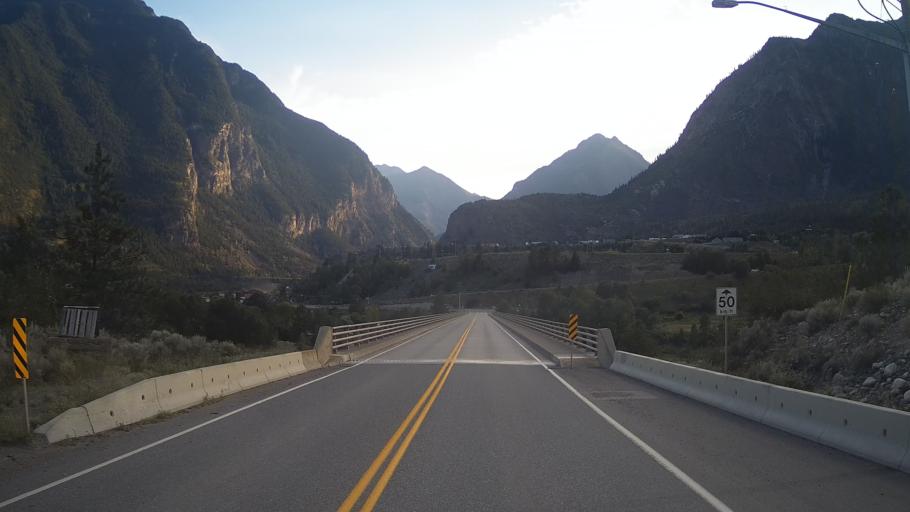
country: CA
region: British Columbia
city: Lillooet
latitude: 50.6846
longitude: -121.9265
